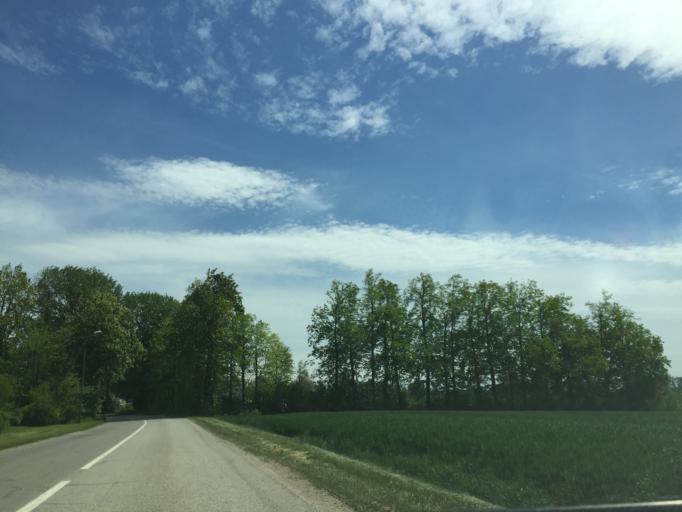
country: LT
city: Linkuva
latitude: 56.0515
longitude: 24.1064
